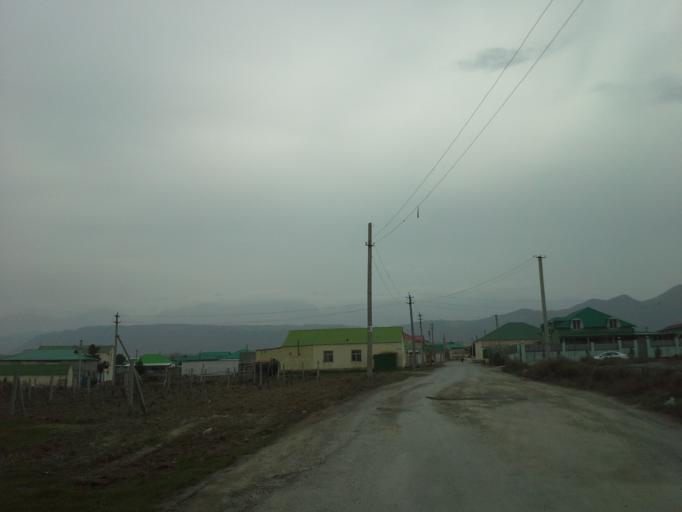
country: TM
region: Ahal
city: Abadan
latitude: 37.9813
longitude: 58.2252
